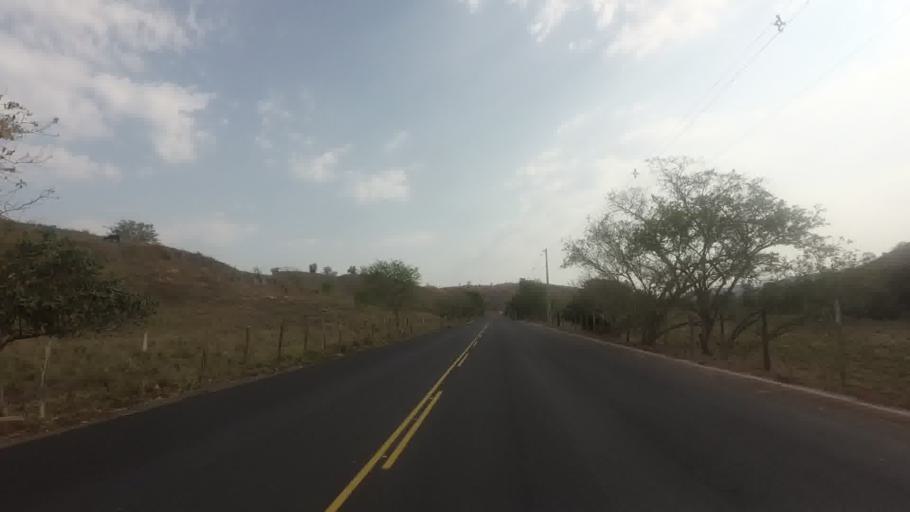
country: BR
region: Rio de Janeiro
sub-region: Itaperuna
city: Itaperuna
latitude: -21.3049
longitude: -41.8489
